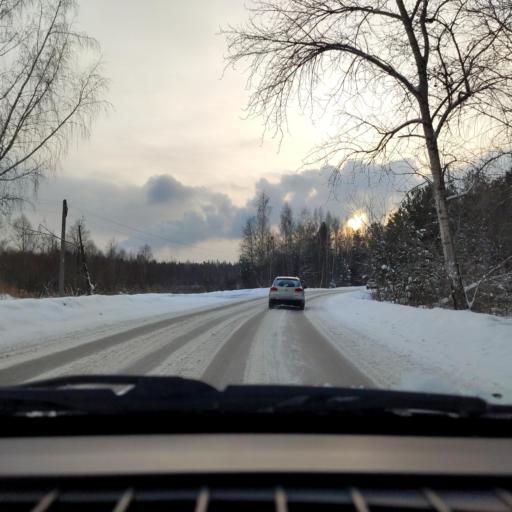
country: RU
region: Perm
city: Overyata
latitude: 58.0479
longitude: 55.8852
